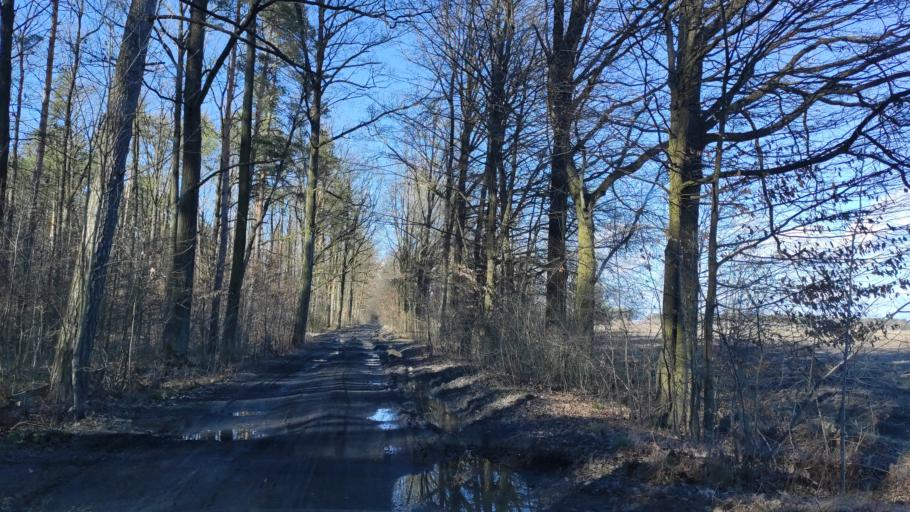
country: PL
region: Masovian Voivodeship
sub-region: Powiat radomski
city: Jedlnia-Letnisko
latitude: 51.4530
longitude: 21.3254
